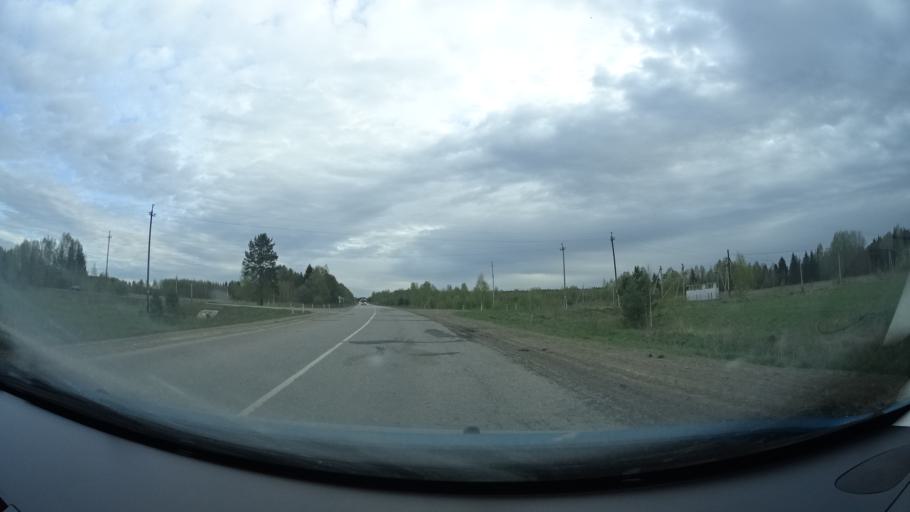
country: RU
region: Perm
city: Osa
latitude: 57.3673
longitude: 55.6055
